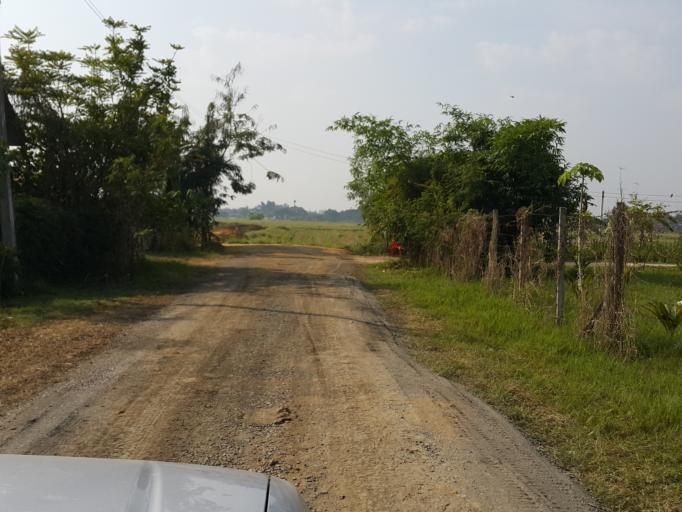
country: TH
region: Chiang Mai
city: San Kamphaeng
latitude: 18.7765
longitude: 99.0979
